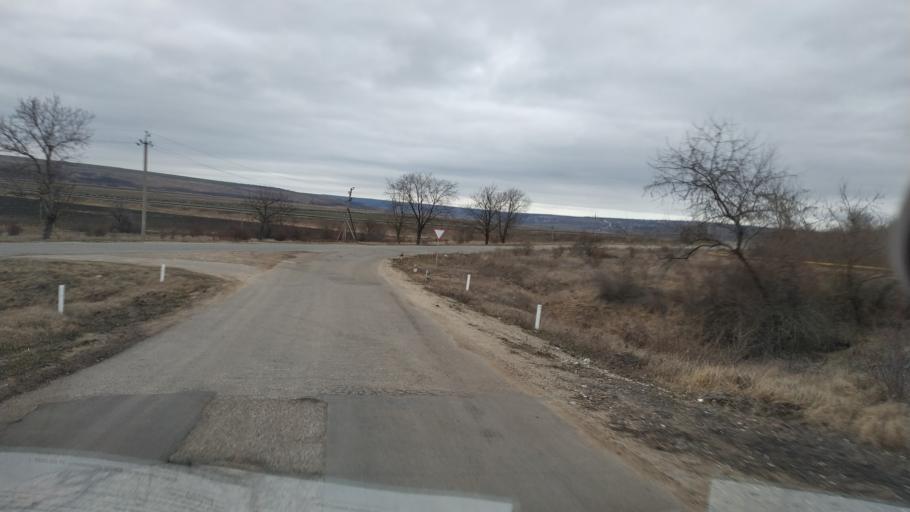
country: MD
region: Causeni
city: Causeni
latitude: 46.6683
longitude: 29.4623
